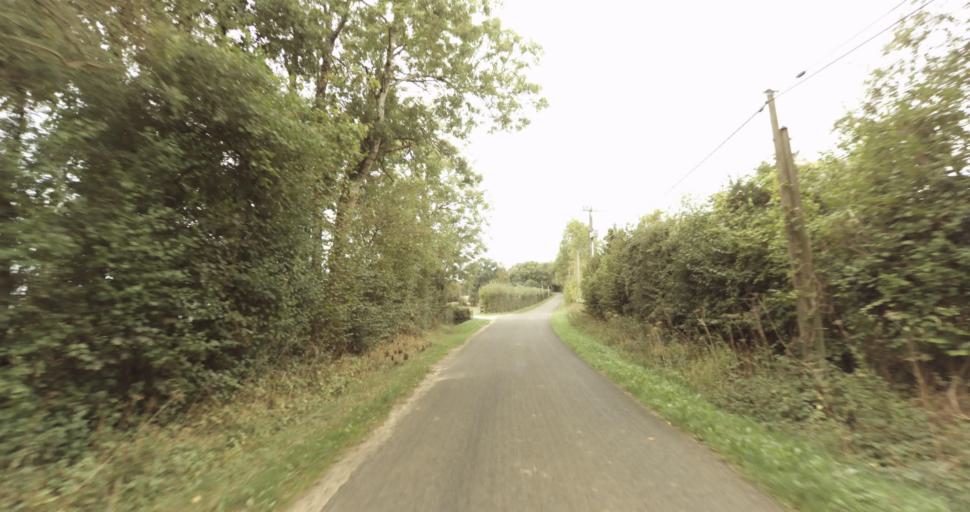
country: FR
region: Lower Normandy
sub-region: Departement de l'Orne
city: Gace
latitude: 48.7198
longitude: 0.3117
